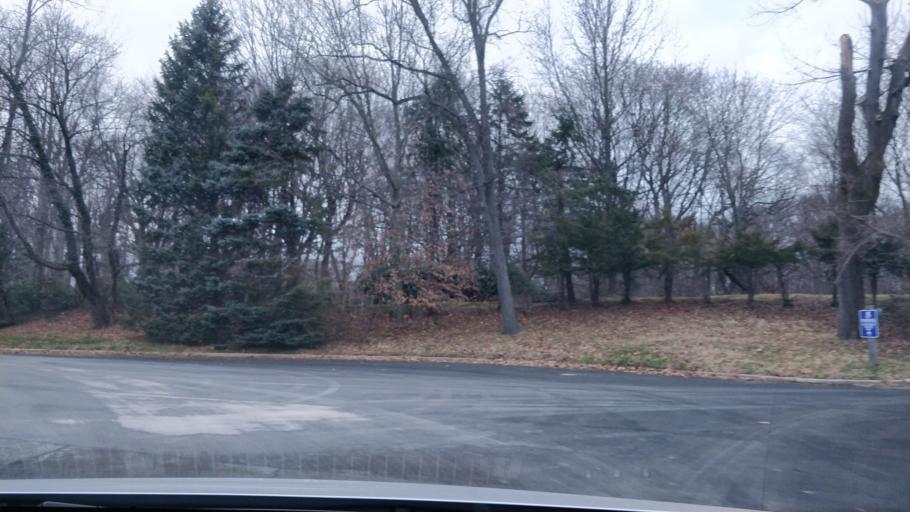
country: US
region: New York
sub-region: Nassau County
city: Oyster Bay Cove
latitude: 40.8870
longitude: -73.4996
